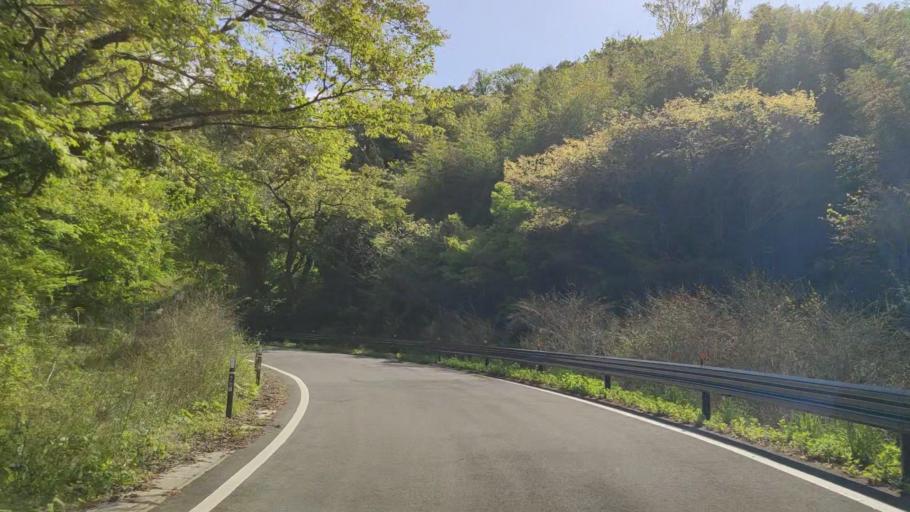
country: JP
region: Miyagi
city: Matsushima
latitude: 38.3400
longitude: 141.1553
